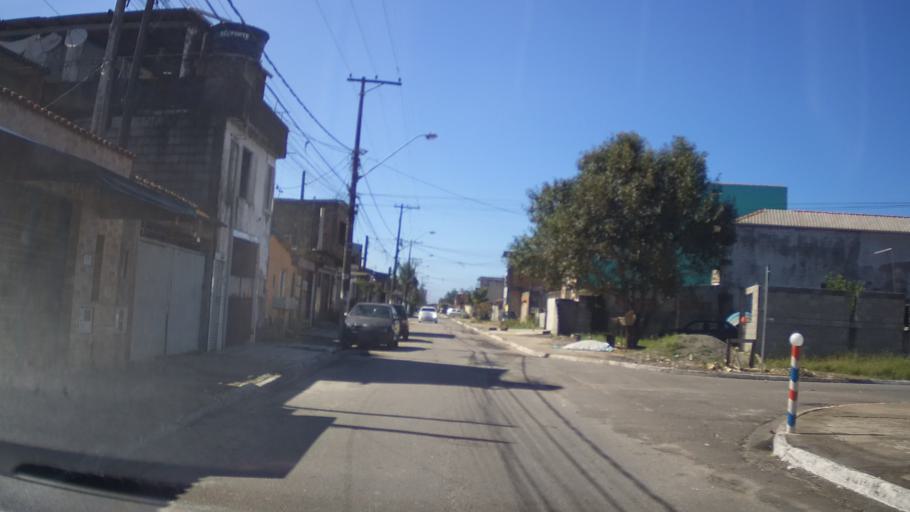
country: BR
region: Sao Paulo
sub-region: Praia Grande
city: Praia Grande
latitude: -24.0311
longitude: -46.5185
